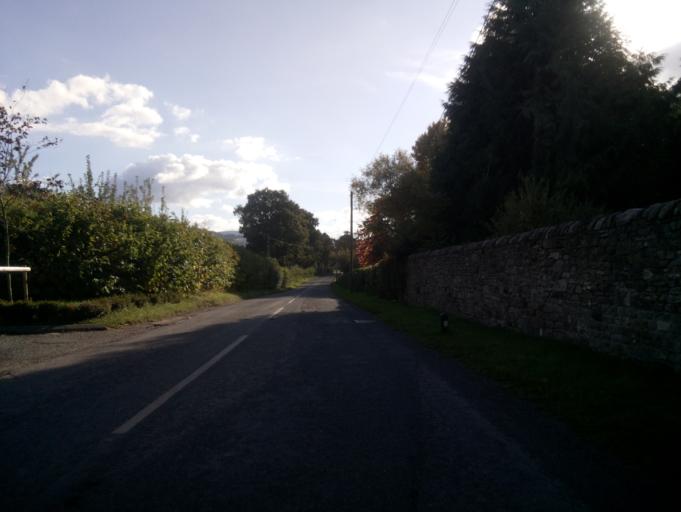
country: GB
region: Wales
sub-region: Sir Powys
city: Hay
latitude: 52.0862
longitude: -3.1177
